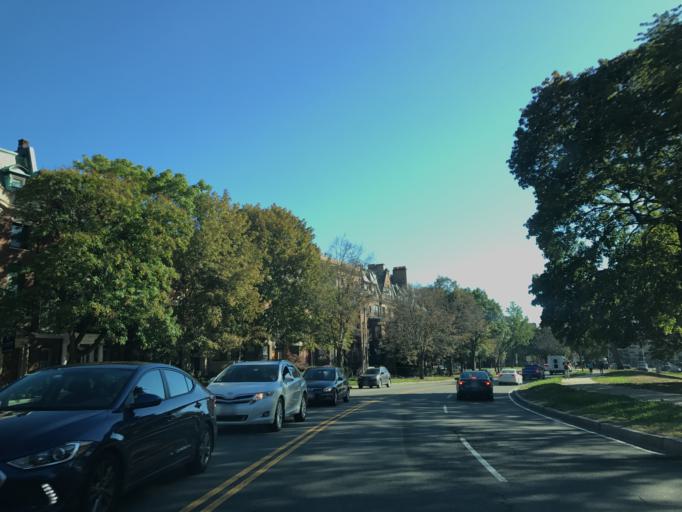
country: US
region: Massachusetts
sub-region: Middlesex County
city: Cambridge
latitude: 42.3459
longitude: -71.0907
